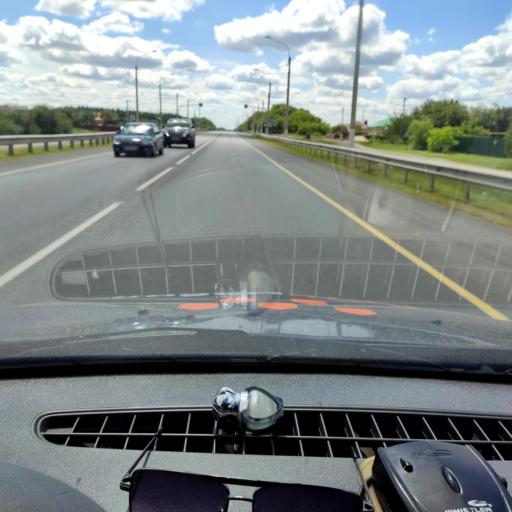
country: RU
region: Lipetsk
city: Khlevnoye
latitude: 52.2570
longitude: 39.1516
